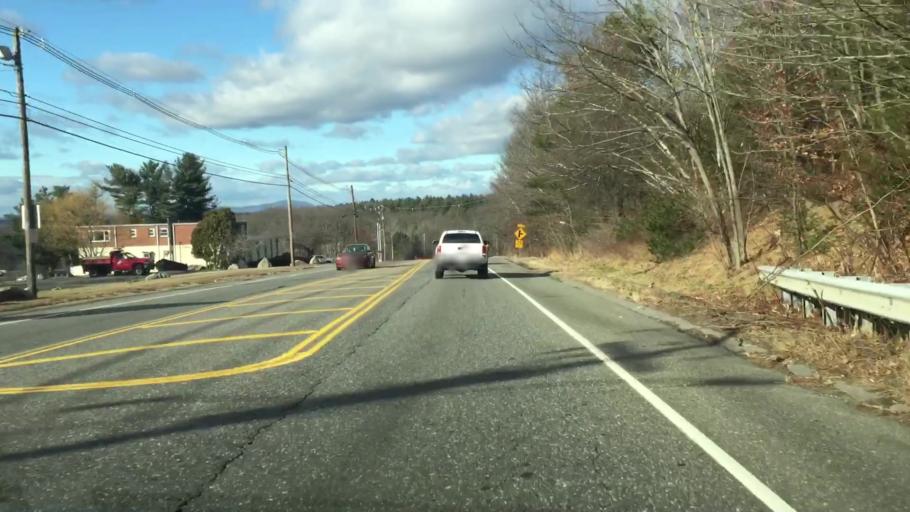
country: US
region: Massachusetts
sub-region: Worcester County
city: Shrewsbury
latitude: 42.3300
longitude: -71.7240
